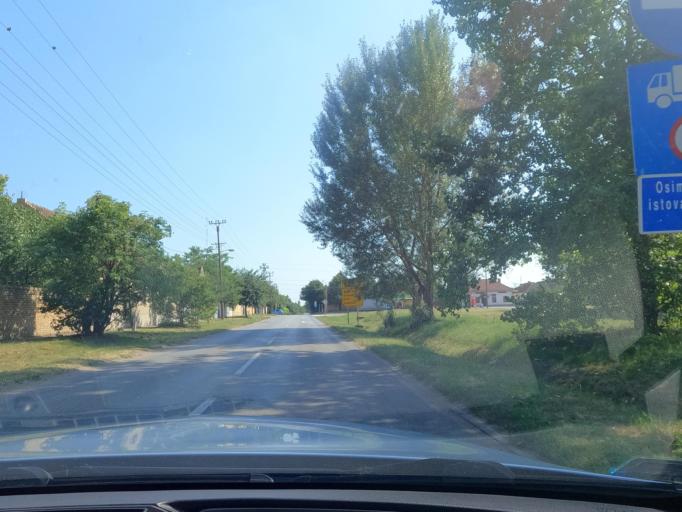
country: RS
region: Autonomna Pokrajina Vojvodina
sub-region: Severnobacki Okrug
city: Backa Topola
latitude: 45.8106
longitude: 19.6443
